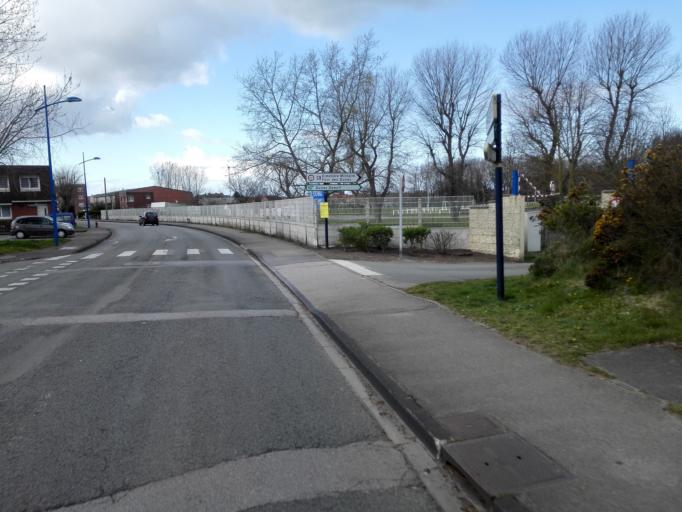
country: FR
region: Nord-Pas-de-Calais
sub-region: Departement du Nord
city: Leffrinckoucke
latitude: 51.0520
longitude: 2.4452
